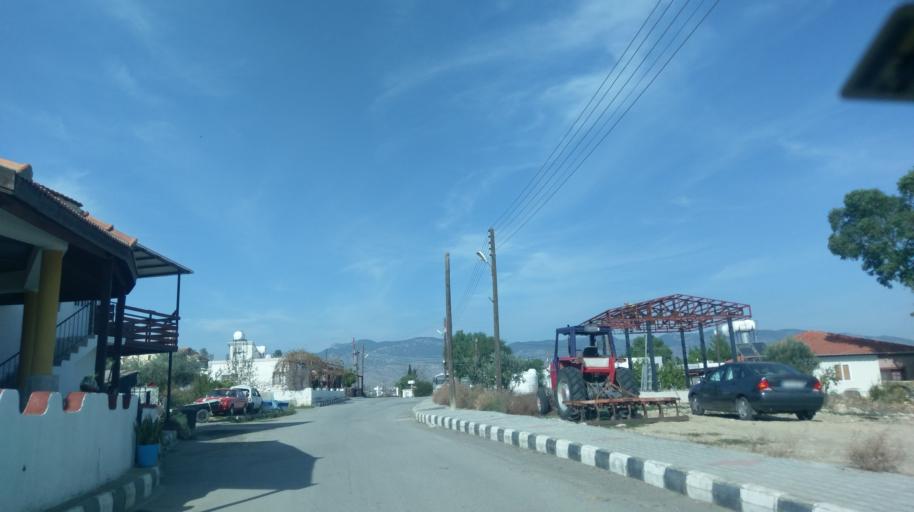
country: CY
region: Ammochostos
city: Lefkonoiko
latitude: 35.2233
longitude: 33.6174
